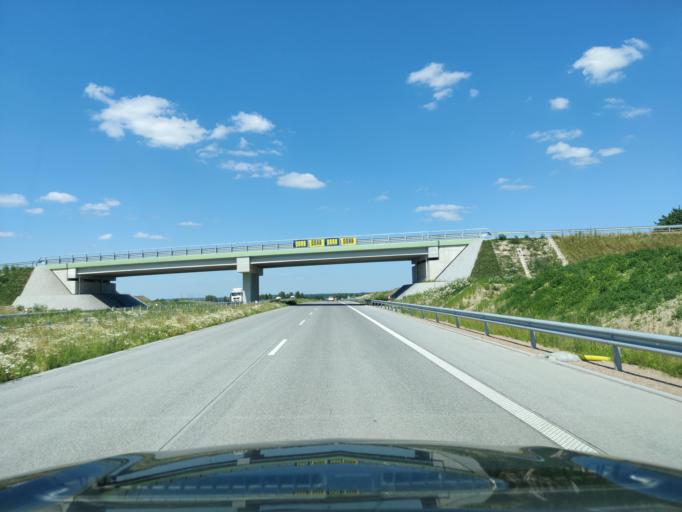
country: PL
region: Masovian Voivodeship
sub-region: Powiat mlawski
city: Wisniewo
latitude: 53.0603
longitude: 20.3659
